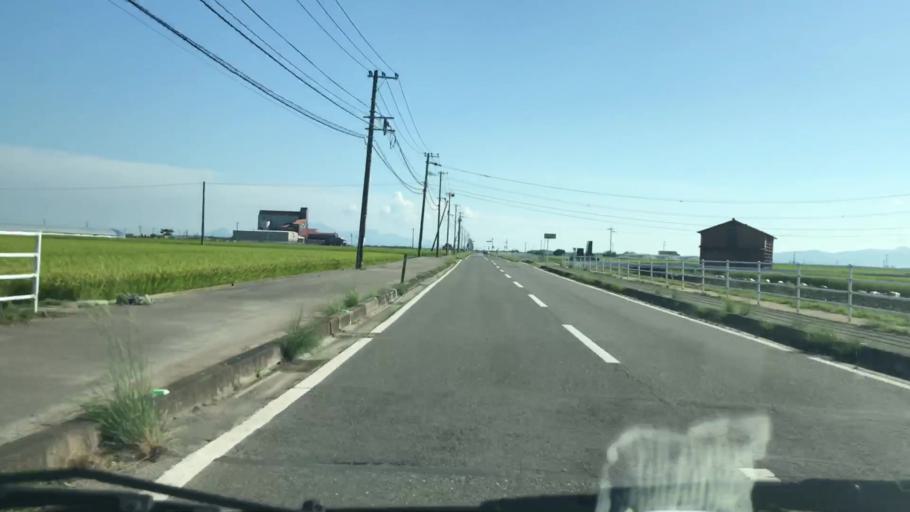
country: JP
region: Saga Prefecture
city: Okawa
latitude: 33.1786
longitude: 130.3126
